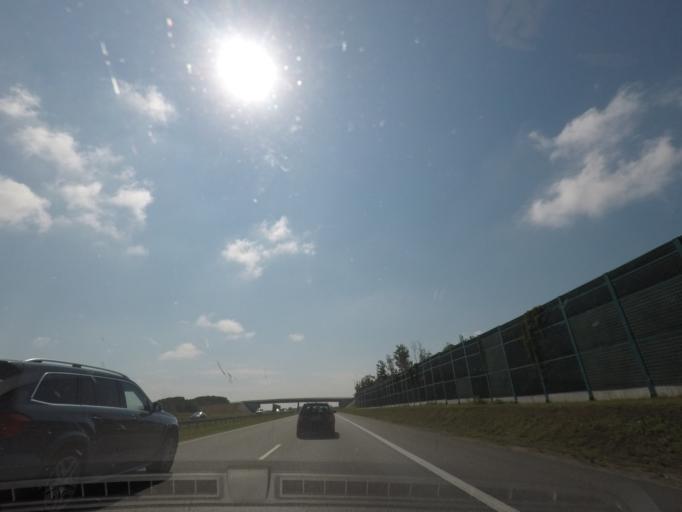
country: PL
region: Lodz Voivodeship
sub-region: Powiat kutnowski
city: Lanieta
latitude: 52.4146
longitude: 19.2645
